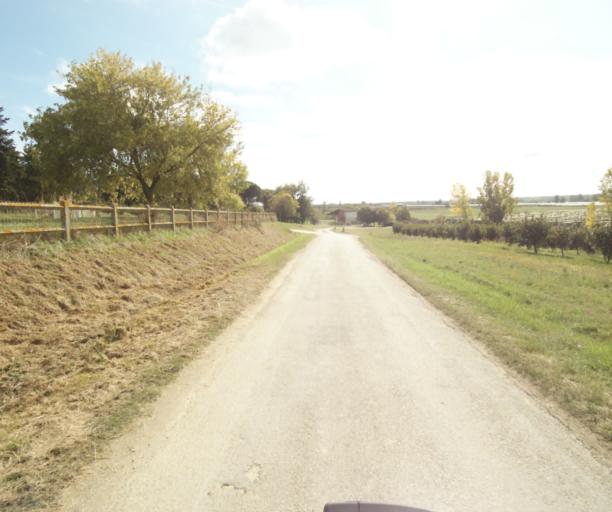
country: FR
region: Midi-Pyrenees
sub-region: Departement du Tarn-et-Garonne
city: Montech
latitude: 43.9490
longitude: 1.2075
